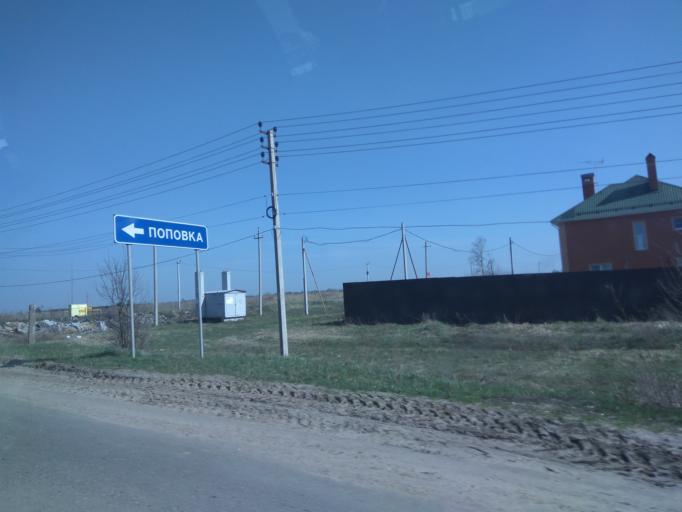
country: RU
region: Moskovskaya
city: Ramenskoye
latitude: 55.5714
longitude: 38.2929
